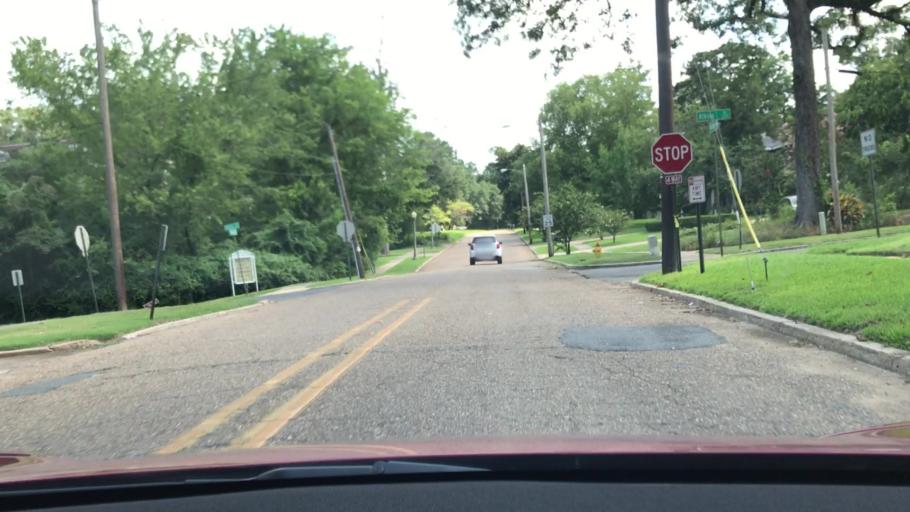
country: US
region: Louisiana
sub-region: Bossier Parish
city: Bossier City
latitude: 32.4810
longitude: -93.7339
